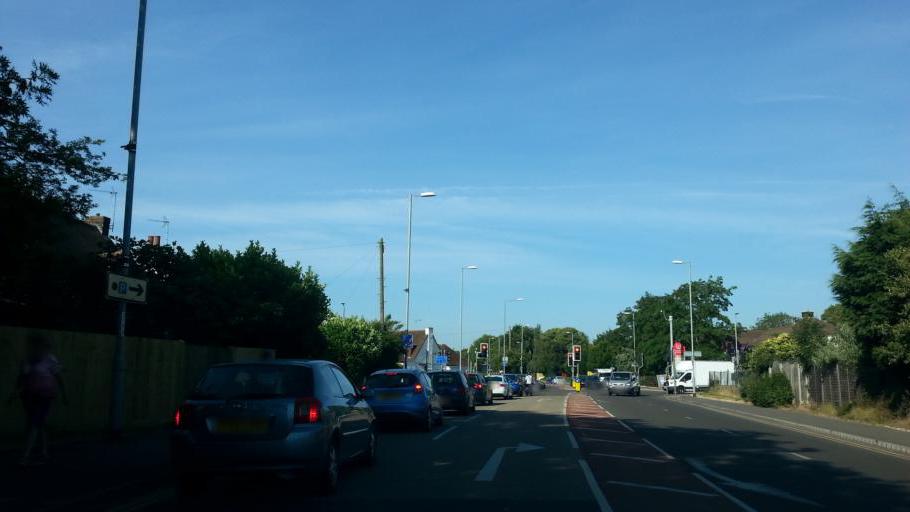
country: GB
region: England
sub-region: Derbyshire
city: Long Eaton
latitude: 52.9182
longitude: -1.2238
